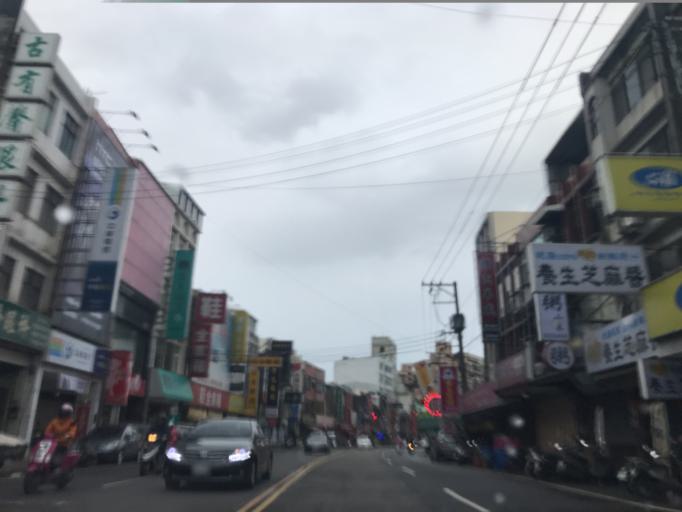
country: TW
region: Taiwan
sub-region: Hsinchu
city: Zhubei
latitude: 24.8352
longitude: 121.0132
